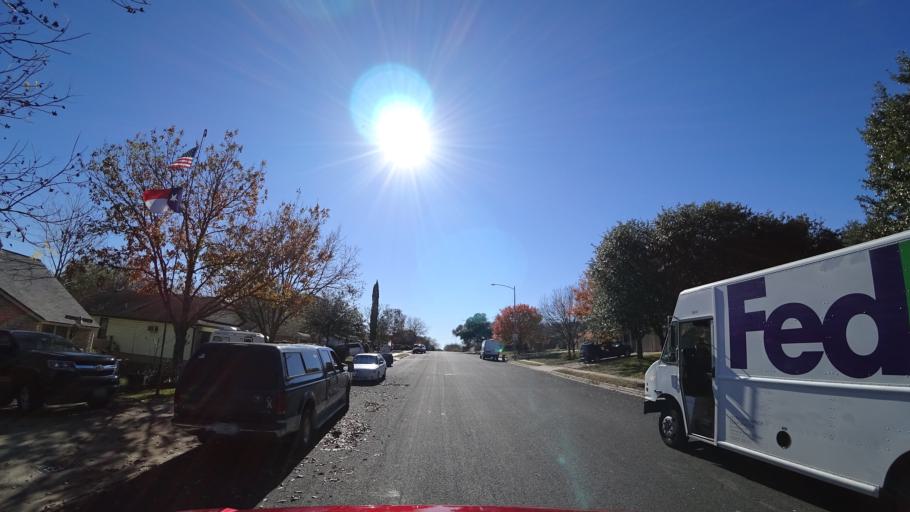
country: US
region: Texas
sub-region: Travis County
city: Wells Branch
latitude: 30.4236
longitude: -97.6864
